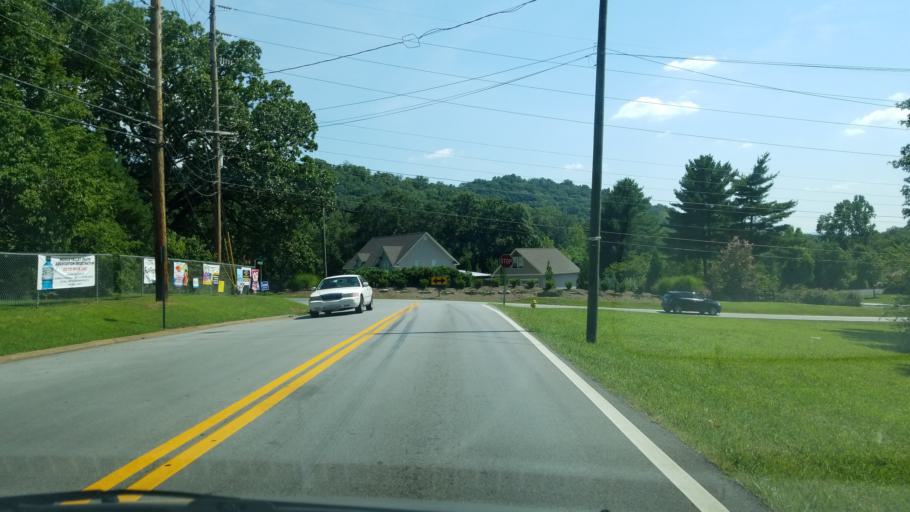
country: US
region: Tennessee
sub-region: Hamilton County
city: Middle Valley
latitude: 35.1296
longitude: -85.2125
